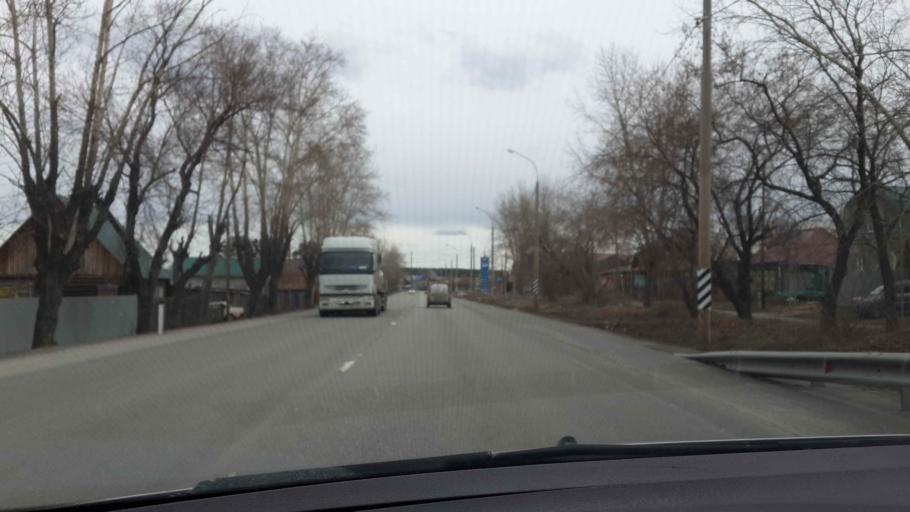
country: RU
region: Sverdlovsk
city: Beloyarskiy
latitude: 56.7567
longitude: 61.3971
